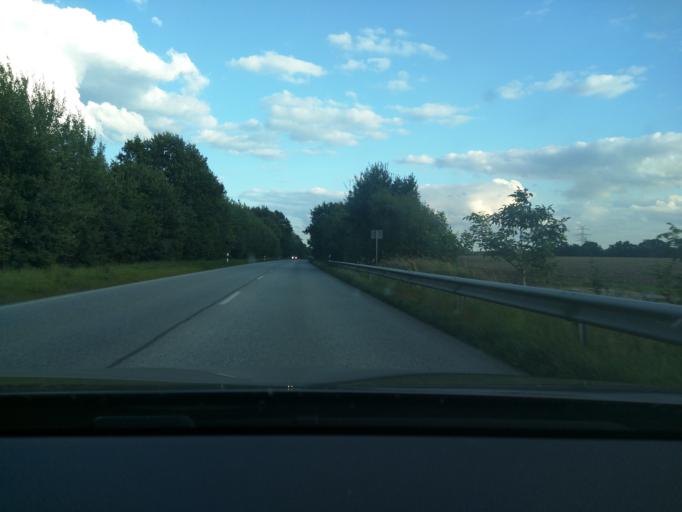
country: DE
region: Schleswig-Holstein
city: Grabau
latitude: 53.4941
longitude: 10.5109
